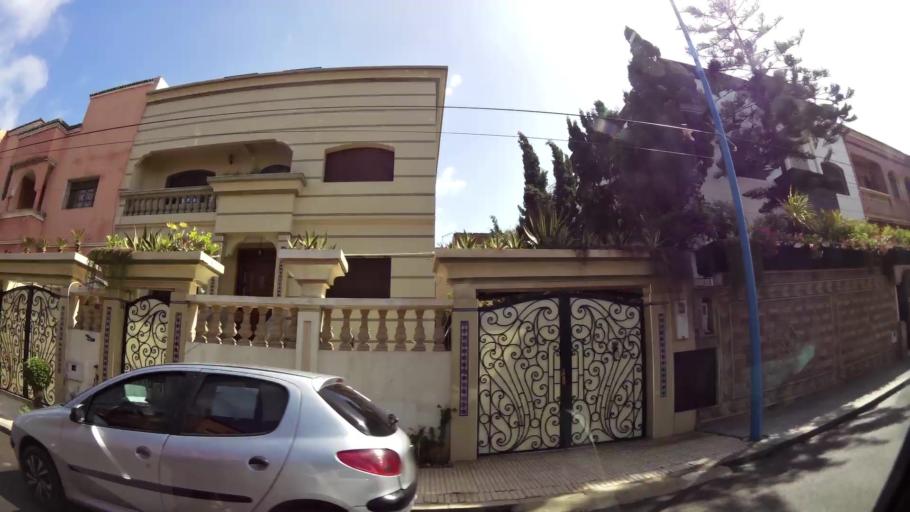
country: MA
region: Grand Casablanca
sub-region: Mediouna
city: Tit Mellil
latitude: 33.6179
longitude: -7.5251
